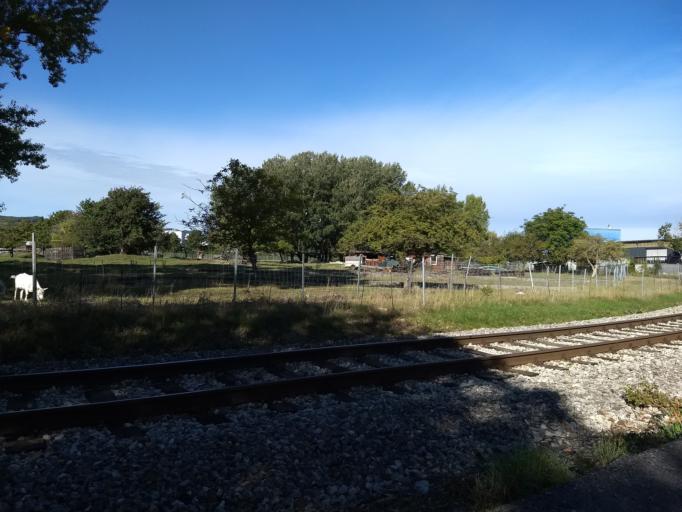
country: AT
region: Lower Austria
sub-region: Politischer Bezirk Modling
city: Neu-Guntramsdorf
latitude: 48.0668
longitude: 16.3288
